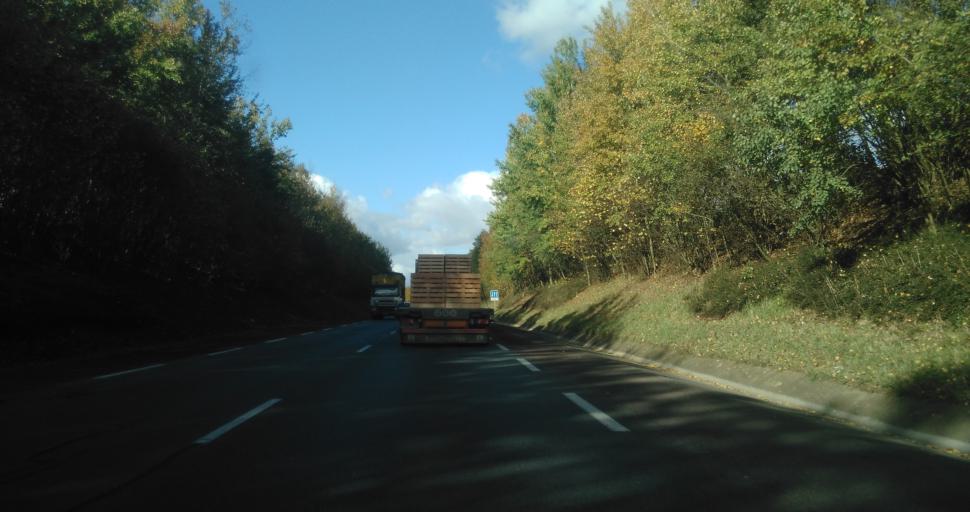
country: FR
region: Nord-Pas-de-Calais
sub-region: Departement du Pas-de-Calais
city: Dainville
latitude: 50.2750
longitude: 2.7080
